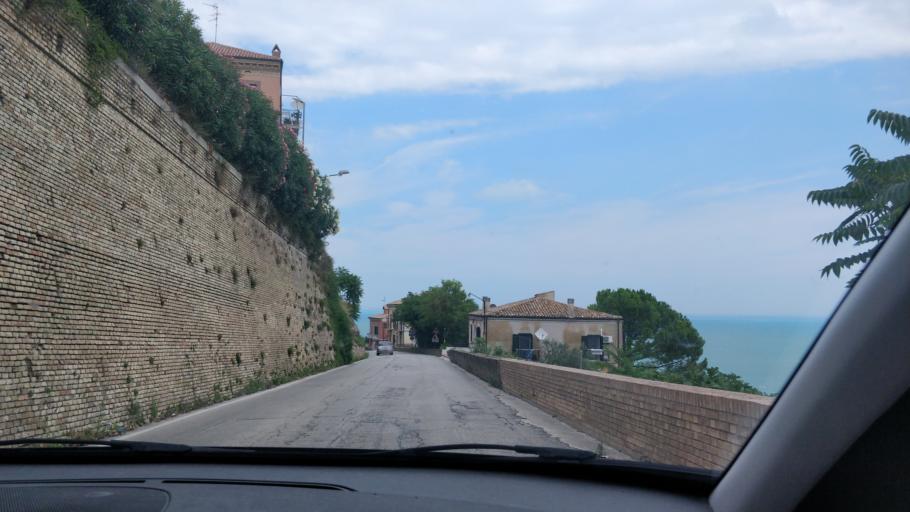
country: IT
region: Abruzzo
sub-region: Provincia di Chieti
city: Marina di San Vito
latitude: 42.3028
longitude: 14.4463
